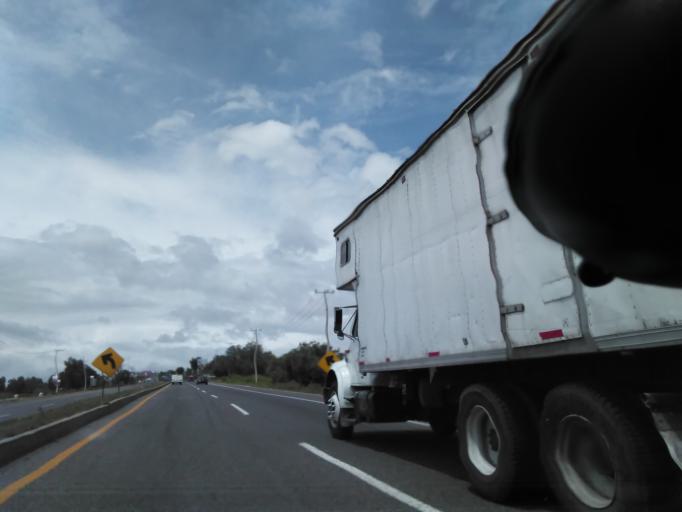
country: MX
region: Hidalgo
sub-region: Atotonilco de Tula
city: Paseos de la Pradera
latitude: 19.9265
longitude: -99.2369
